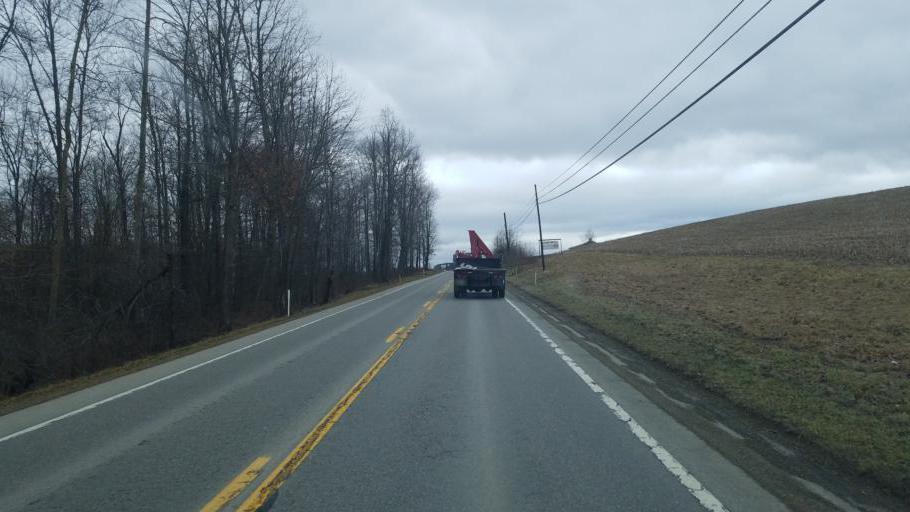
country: US
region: Pennsylvania
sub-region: Clarion County
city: Marianne
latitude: 41.3532
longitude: -79.3306
